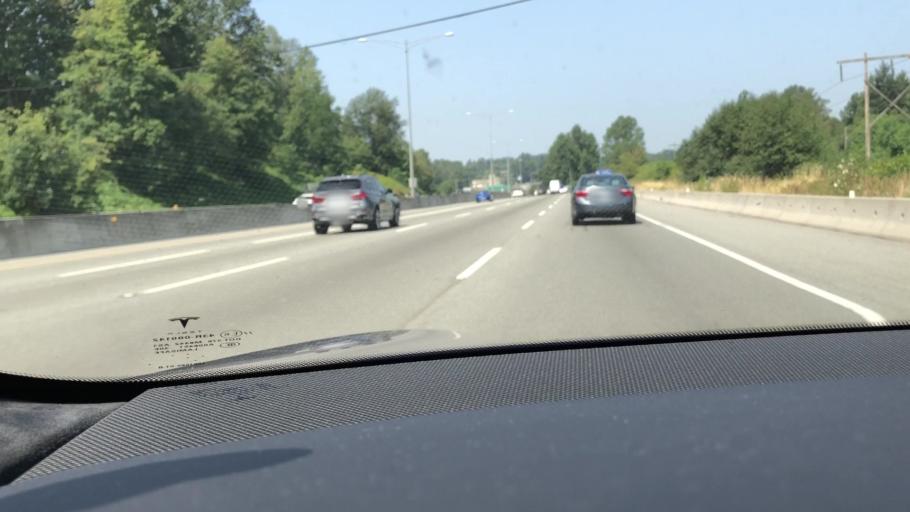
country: CA
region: British Columbia
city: Burnaby
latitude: 49.2399
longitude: -122.9543
